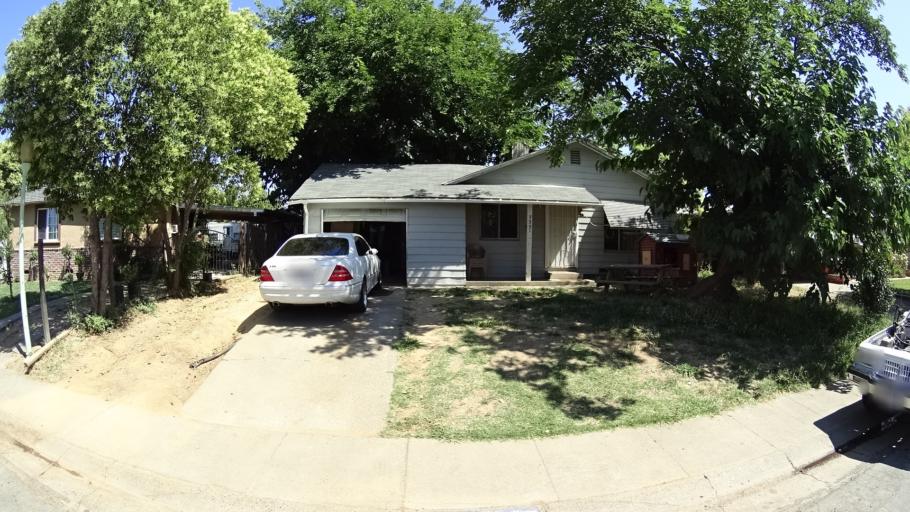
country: US
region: California
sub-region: Sacramento County
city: Florin
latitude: 38.5285
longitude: -121.4182
